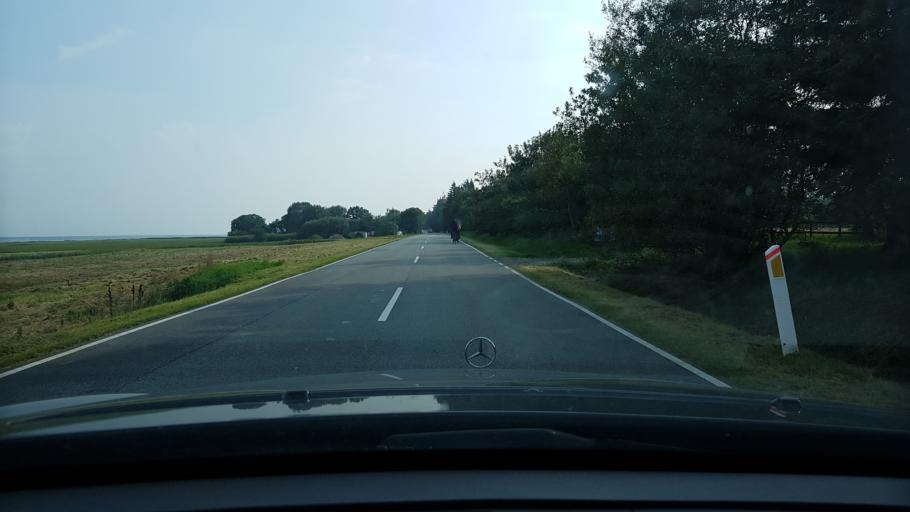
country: DK
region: North Denmark
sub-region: Alborg Kommune
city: Hals
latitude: 56.8814
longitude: 10.2612
